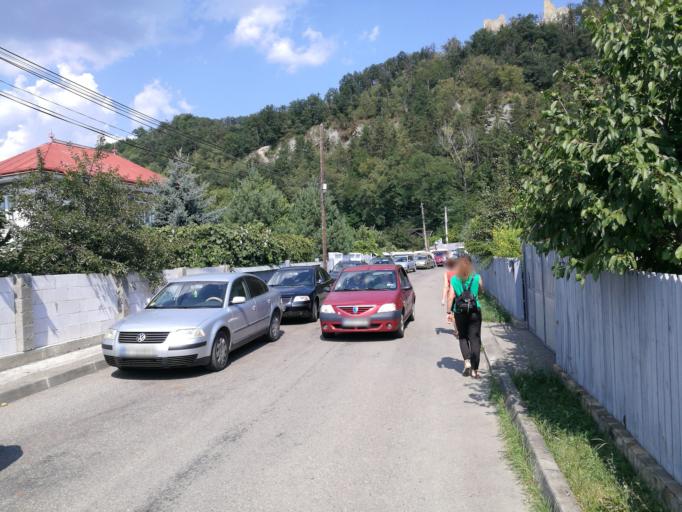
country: RO
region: Neamt
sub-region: Oras Targu Neamt
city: Humulesti
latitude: 47.2118
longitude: 26.3424
